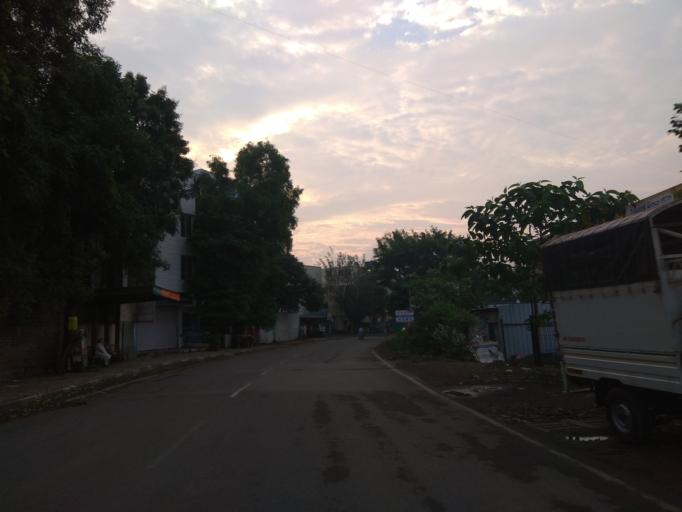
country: IN
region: Maharashtra
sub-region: Pune Division
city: Kharakvasla
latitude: 18.4833
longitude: 73.8042
